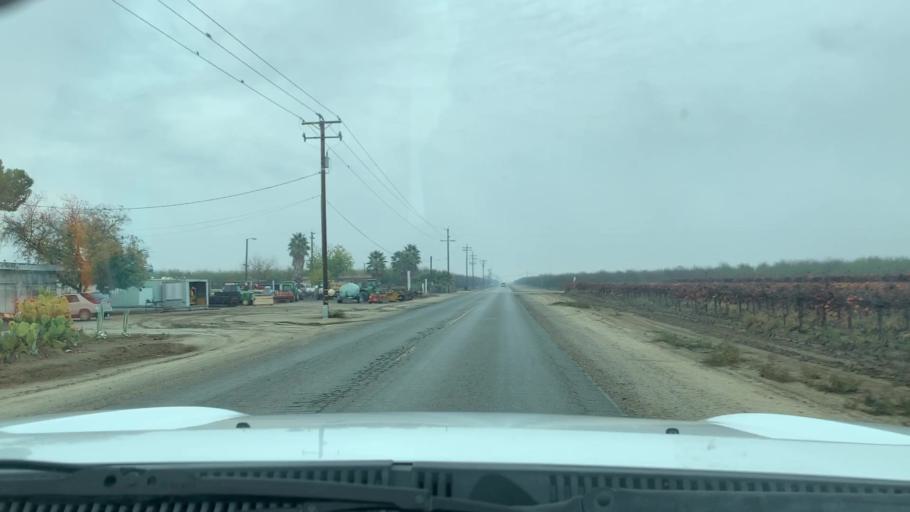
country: US
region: California
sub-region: Kern County
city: Delano
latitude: 35.7611
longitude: -119.3670
